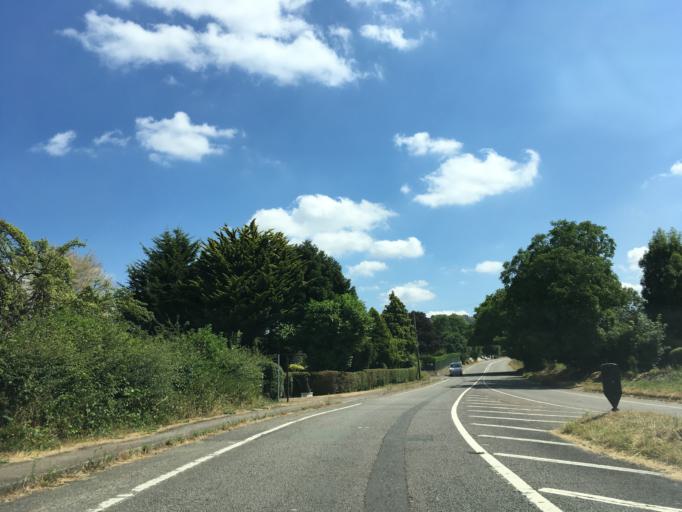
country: GB
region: England
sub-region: Gloucestershire
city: Shurdington
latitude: 51.8412
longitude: -2.1374
